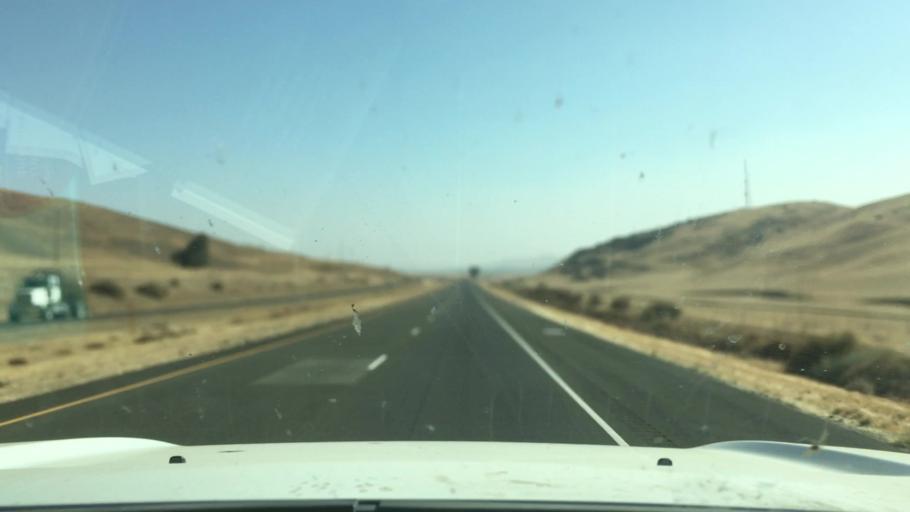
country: US
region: California
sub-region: San Luis Obispo County
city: Shandon
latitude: 35.7209
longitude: -120.1830
